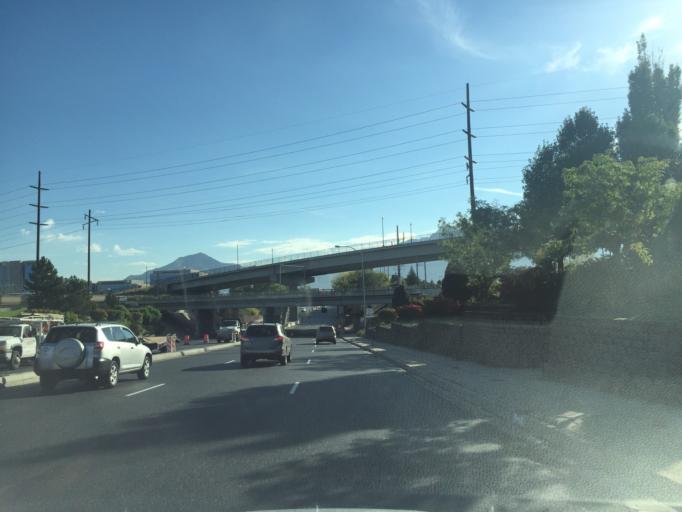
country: US
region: Utah
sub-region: Salt Lake County
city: Murray
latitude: 40.6548
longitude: -111.8996
